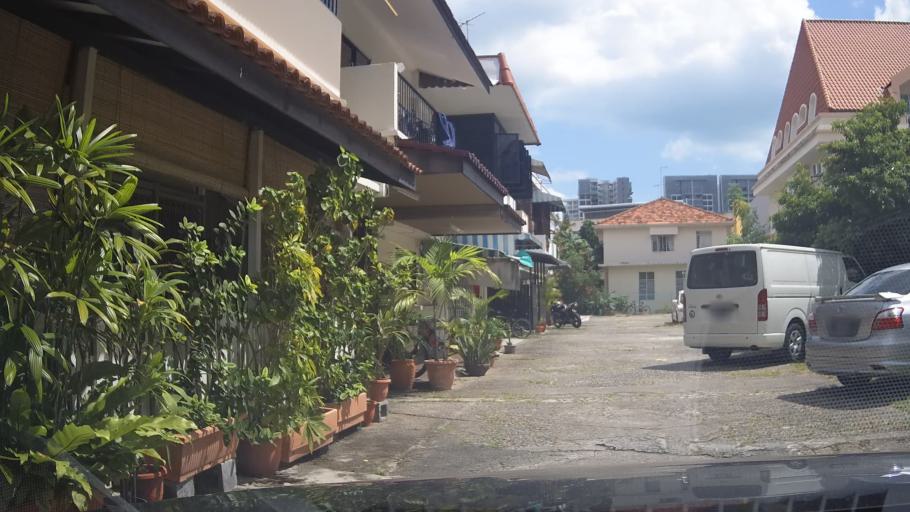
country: SG
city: Singapore
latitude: 1.3070
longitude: 103.9003
